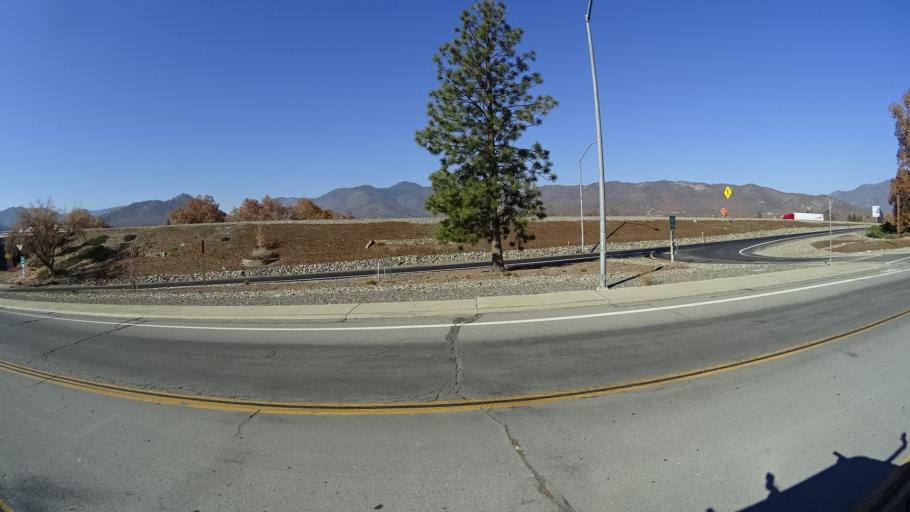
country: US
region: California
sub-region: Siskiyou County
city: Yreka
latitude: 41.7313
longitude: -122.6319
